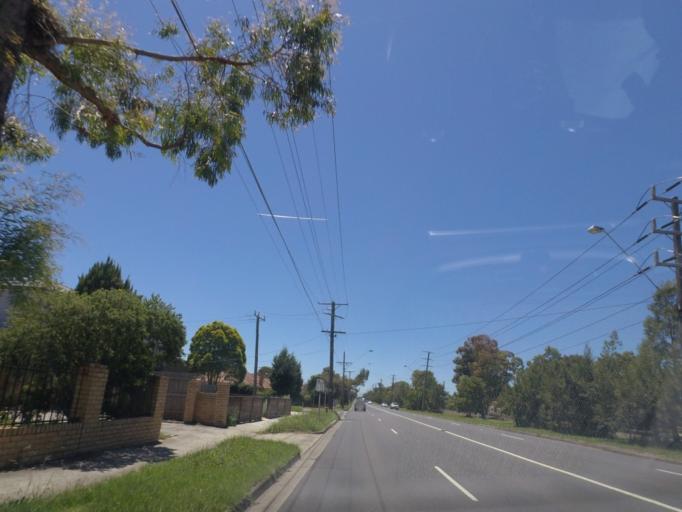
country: AU
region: Victoria
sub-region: Darebin
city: Reservoir
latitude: -37.7037
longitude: 145.0099
